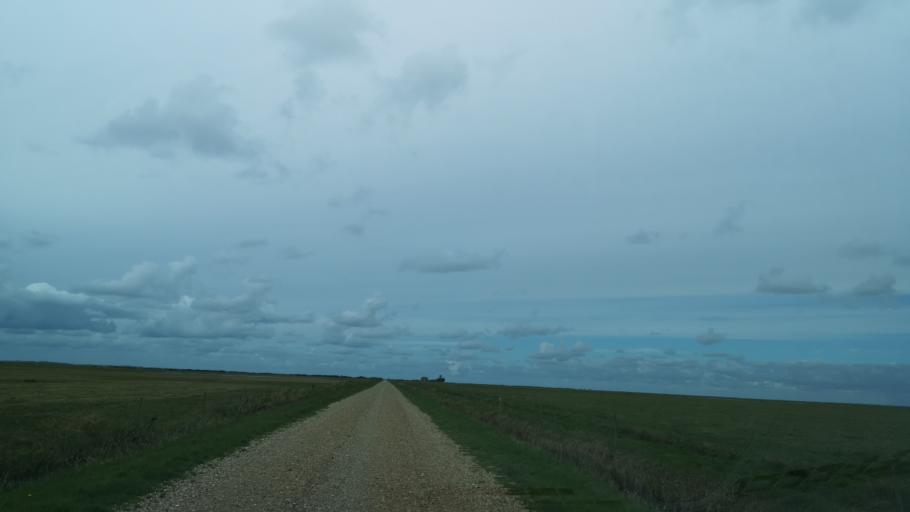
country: DK
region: Central Jutland
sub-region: Ringkobing-Skjern Kommune
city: Hvide Sande
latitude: 55.8838
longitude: 8.2209
